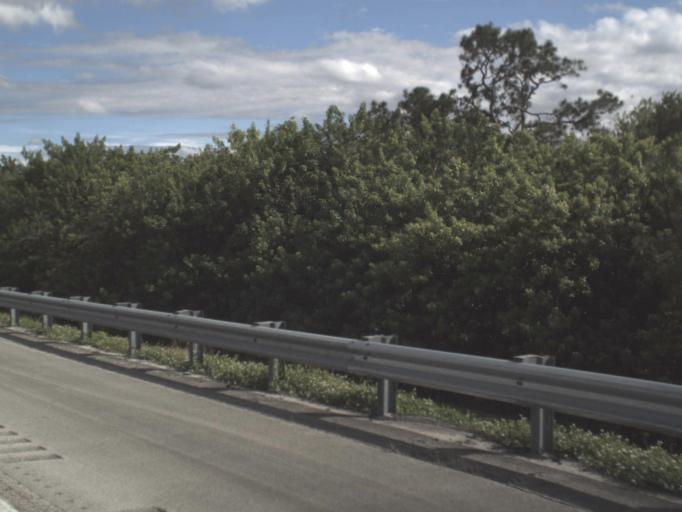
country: US
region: Florida
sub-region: Saint Lucie County
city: Lakewood Park
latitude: 27.4843
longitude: -80.4638
